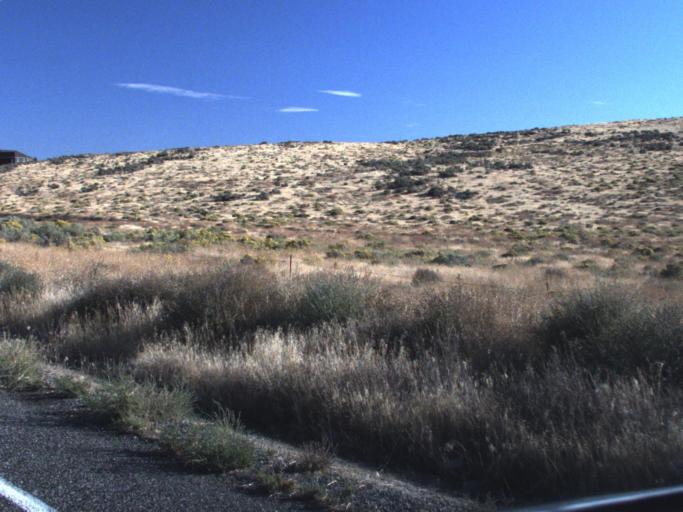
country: US
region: Washington
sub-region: Benton County
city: West Richland
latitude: 46.2909
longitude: -119.3871
